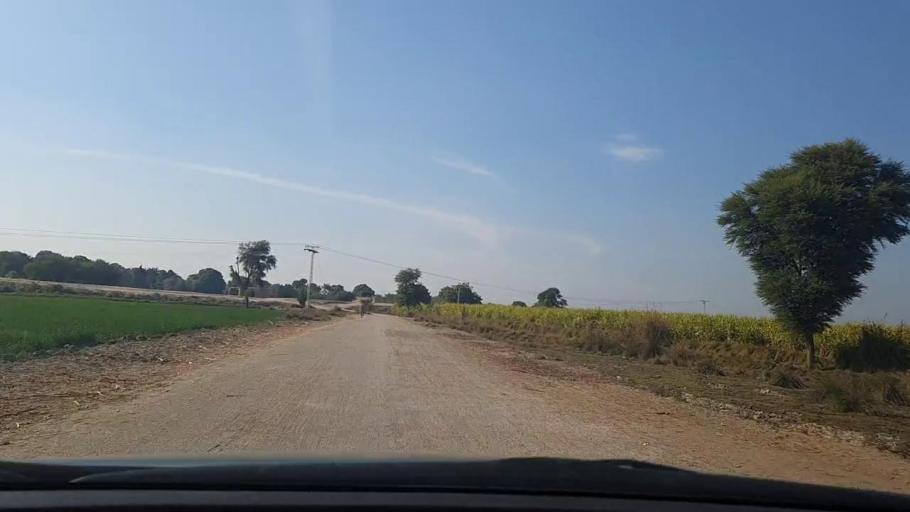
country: PK
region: Sindh
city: Sehwan
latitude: 26.3366
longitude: 67.9790
